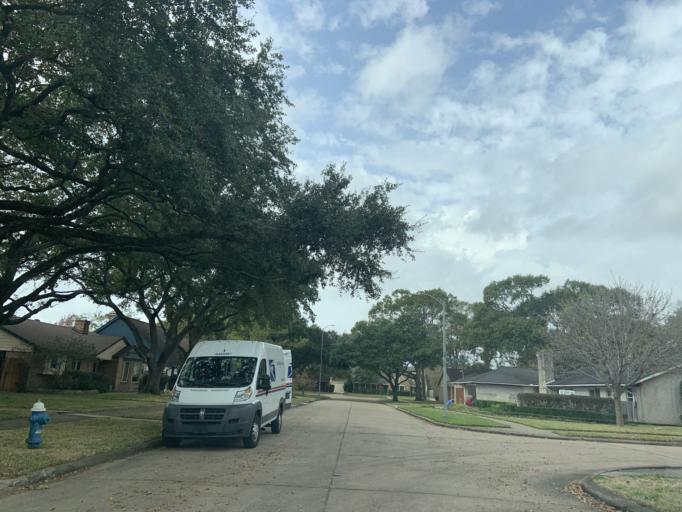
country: US
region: Texas
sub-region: Harris County
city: Bellaire
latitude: 29.6759
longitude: -95.5015
